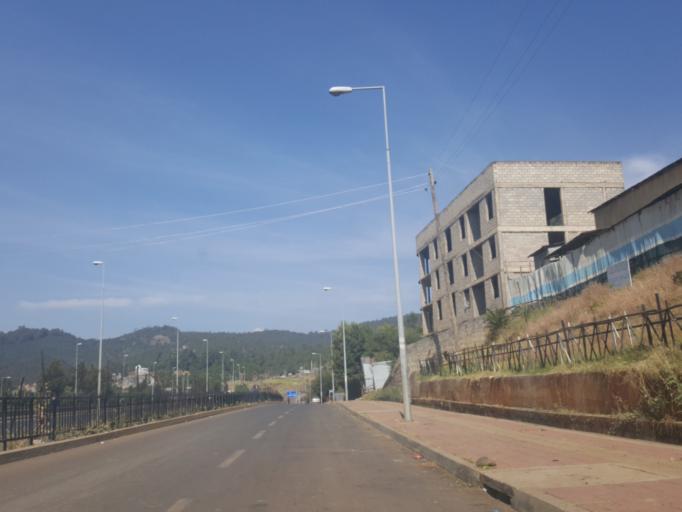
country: ET
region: Adis Abeba
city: Addis Ababa
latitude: 9.0673
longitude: 38.7257
